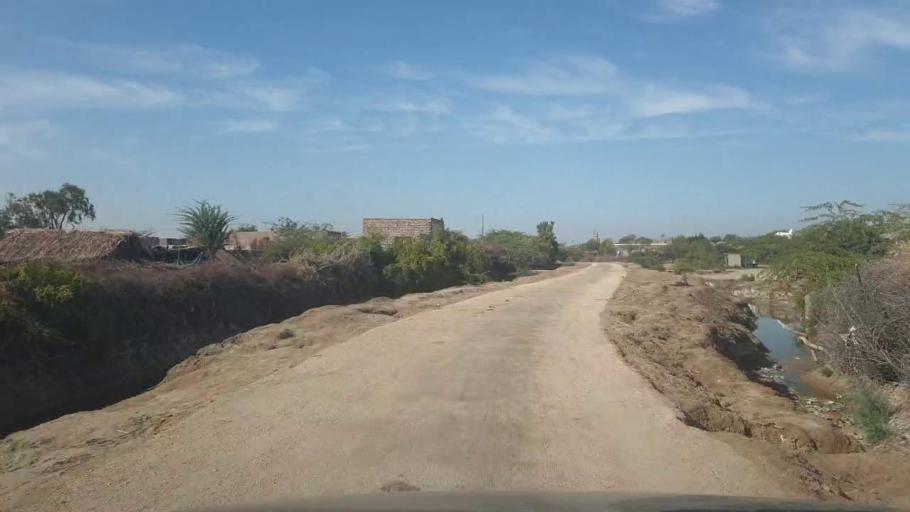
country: PK
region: Sindh
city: Pithoro
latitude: 25.3966
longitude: 69.2515
